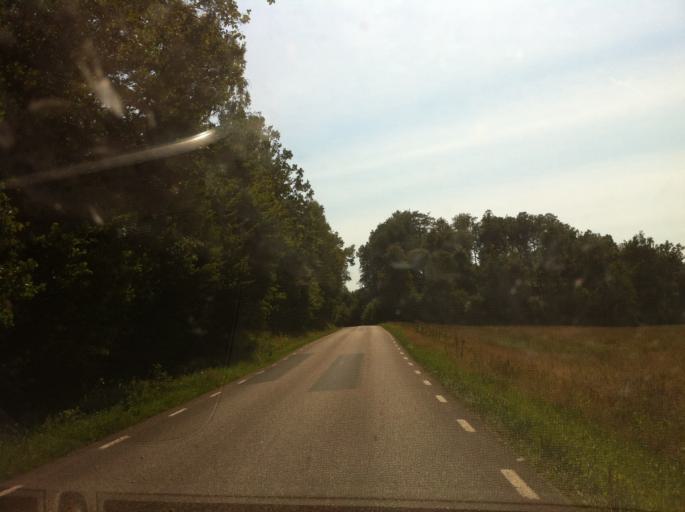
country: SE
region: Skane
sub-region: Hoors Kommun
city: Hoeoer
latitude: 56.0099
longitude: 13.4911
